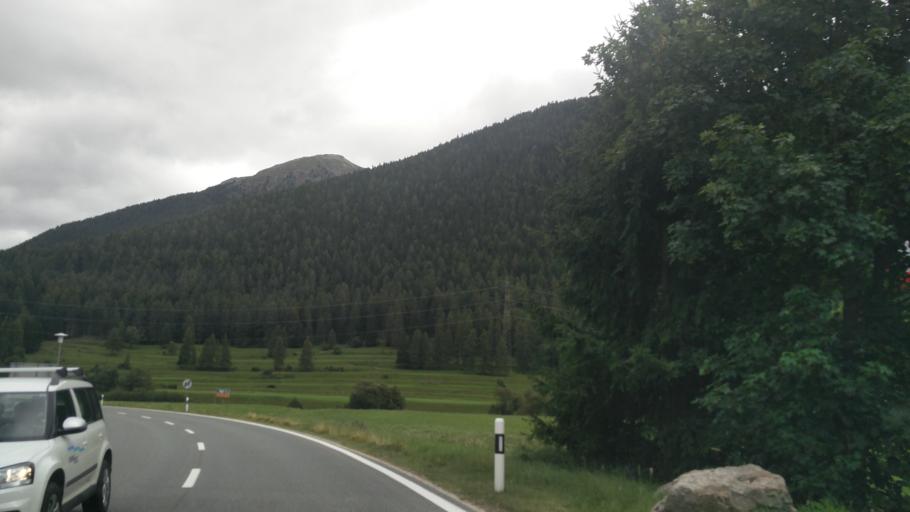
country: CH
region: Grisons
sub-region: Inn District
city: Zernez
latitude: 46.6965
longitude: 10.0988
